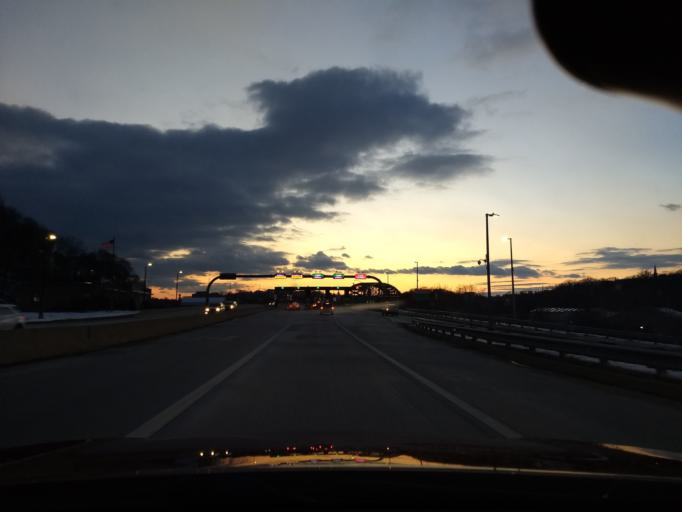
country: US
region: New Jersey
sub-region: Warren County
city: Phillipsburg
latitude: 40.6960
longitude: -75.1984
